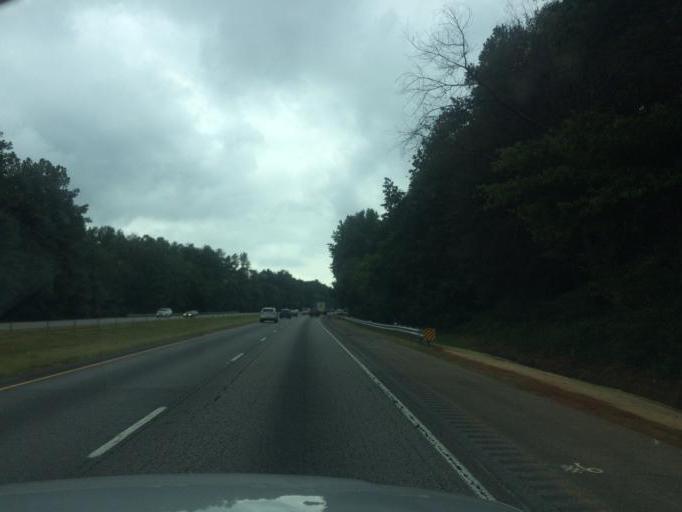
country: US
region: Georgia
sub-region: Banks County
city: Homer
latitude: 34.3176
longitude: -83.3712
